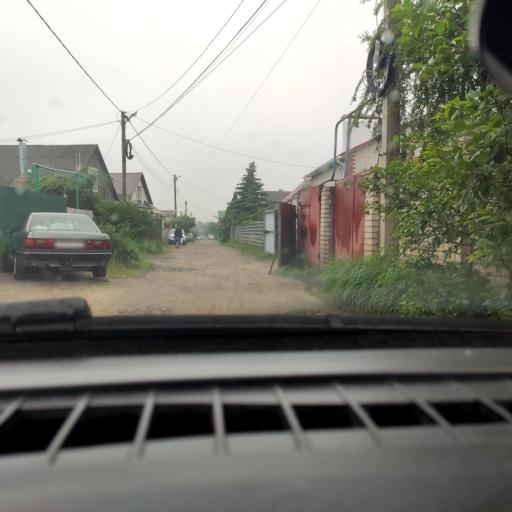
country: RU
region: Voronezj
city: Podgornoye
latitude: 51.7413
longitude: 39.1585
